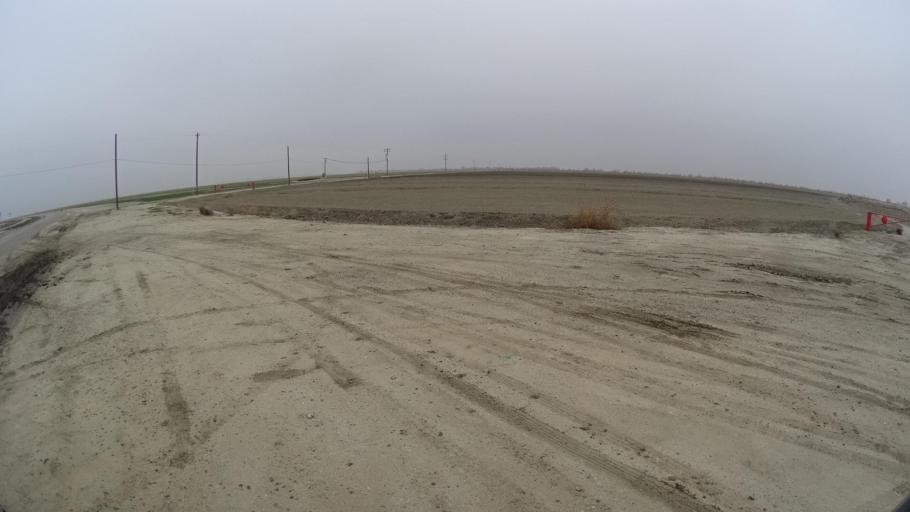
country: US
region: California
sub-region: Kern County
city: Rosedale
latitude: 35.2304
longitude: -119.2540
